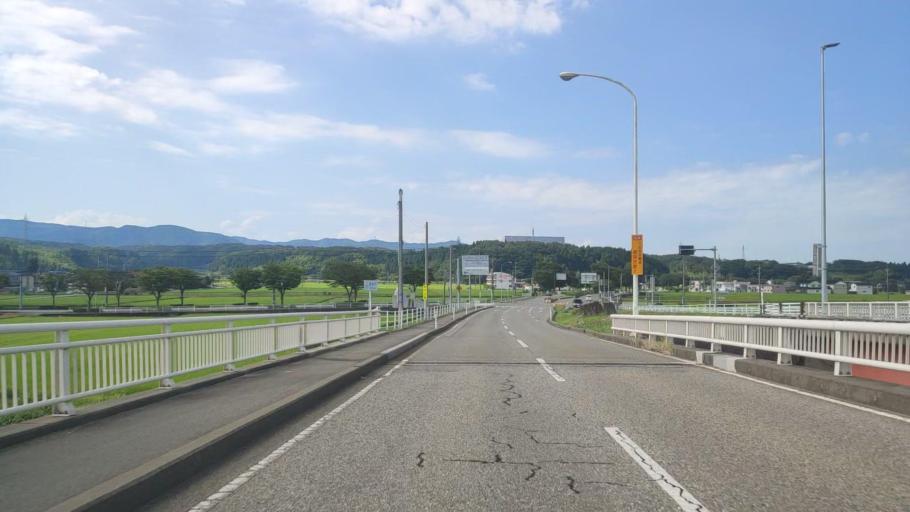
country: JP
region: Ishikawa
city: Tsurugi-asahimachi
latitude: 36.4576
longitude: 136.5756
